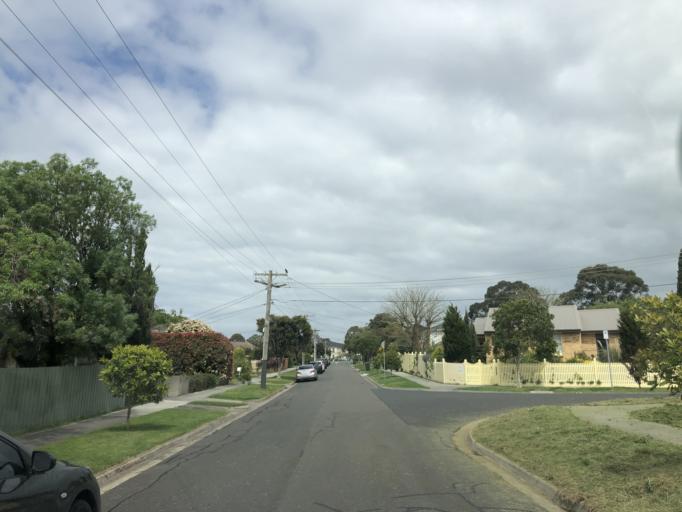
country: AU
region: Victoria
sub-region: Monash
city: Ashwood
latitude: -37.8711
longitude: 145.1081
